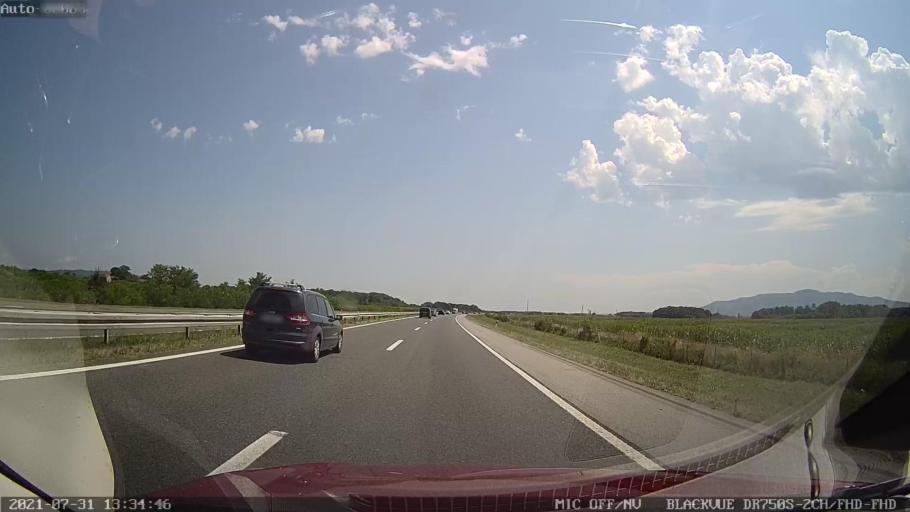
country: HR
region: Brodsko-Posavska
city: Batrina
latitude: 45.1871
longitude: 17.6351
